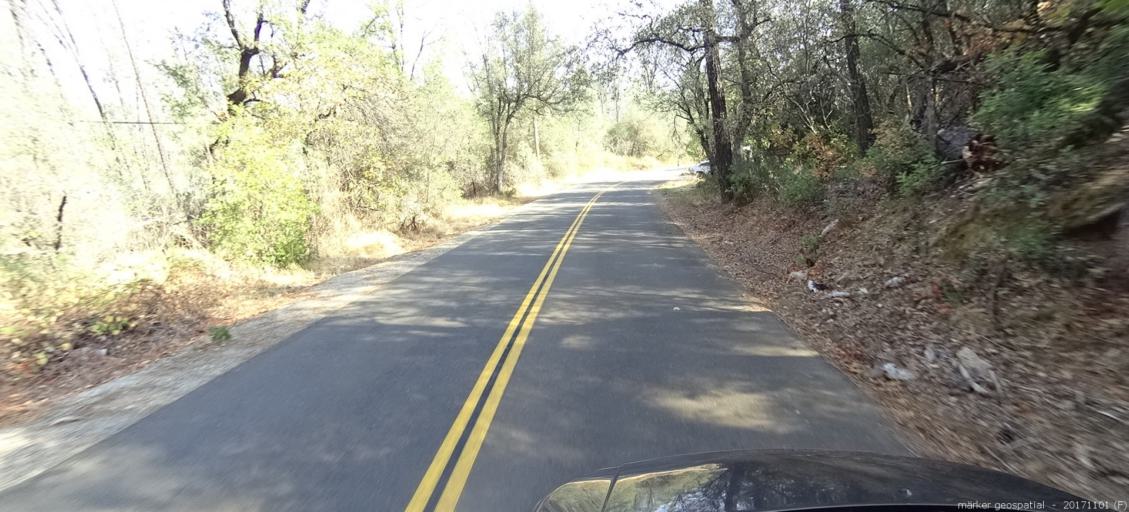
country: US
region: California
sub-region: Shasta County
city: Central Valley (historical)
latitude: 40.6783
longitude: -122.4150
